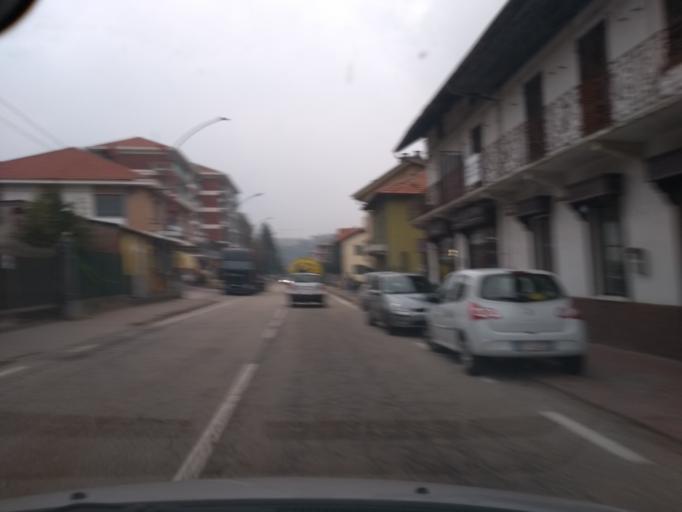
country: IT
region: Piedmont
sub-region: Provincia di Torino
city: Germagnano
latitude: 45.2638
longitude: 7.4707
